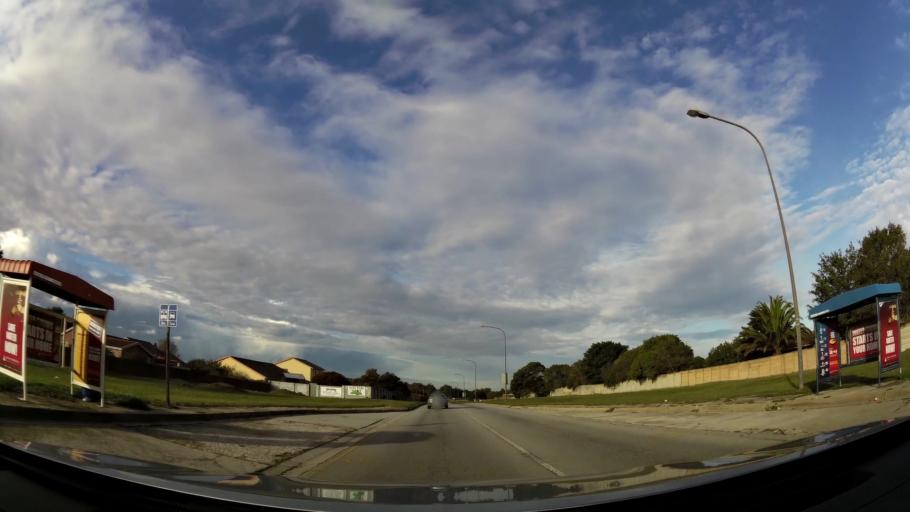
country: ZA
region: Eastern Cape
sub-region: Nelson Mandela Bay Metropolitan Municipality
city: Port Elizabeth
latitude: -33.9591
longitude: 25.4898
